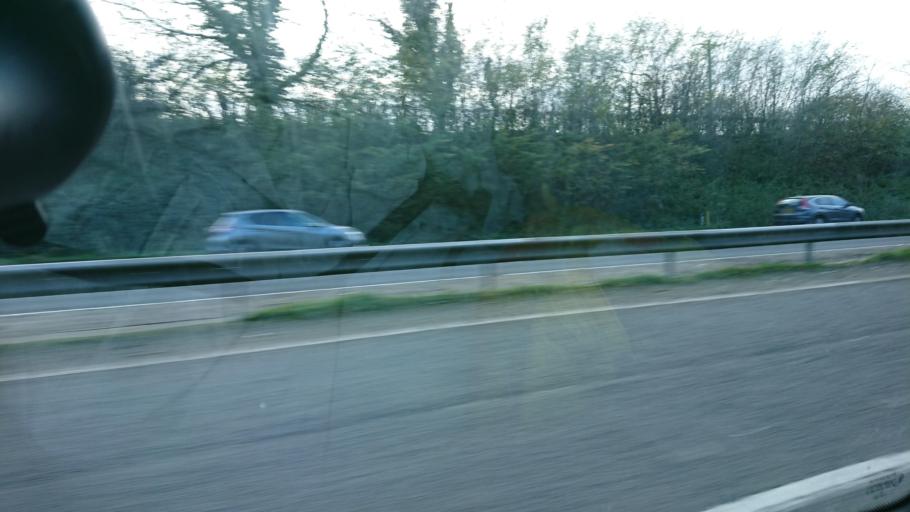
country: GB
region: England
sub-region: Devon
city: Yealmpton
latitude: 50.3797
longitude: -4.0108
